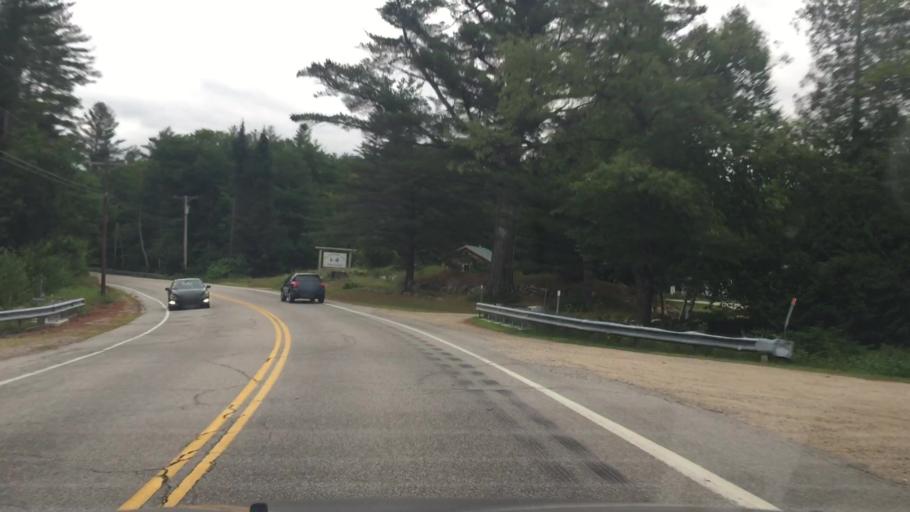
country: US
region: New Hampshire
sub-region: Carroll County
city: North Conway
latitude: 44.0734
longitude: -71.3024
